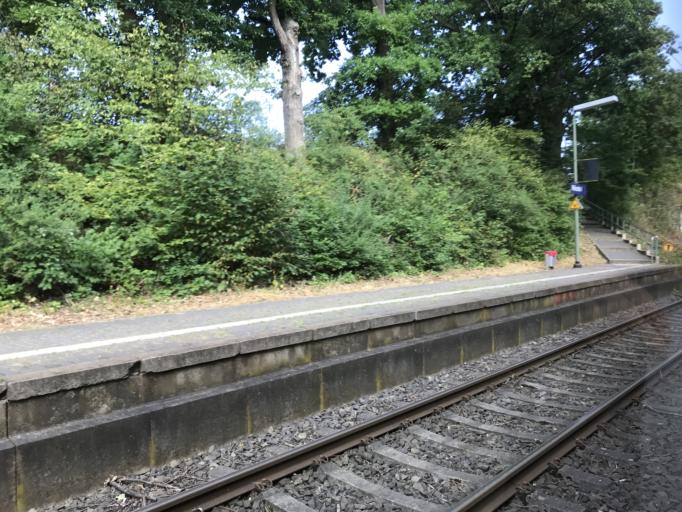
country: DE
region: Hesse
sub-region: Regierungsbezirk Darmstadt
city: Idstein
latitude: 50.2455
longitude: 8.2488
